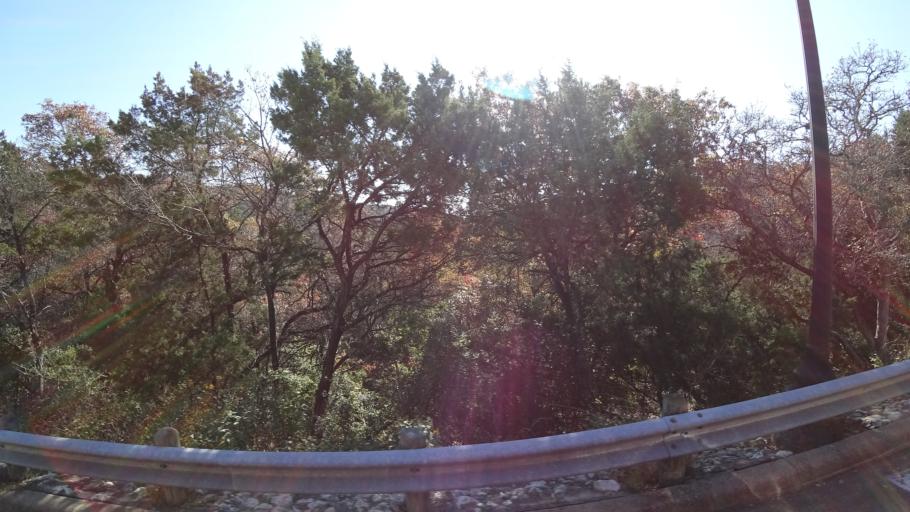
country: US
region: Texas
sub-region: Williamson County
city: Jollyville
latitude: 30.3803
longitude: -97.7686
